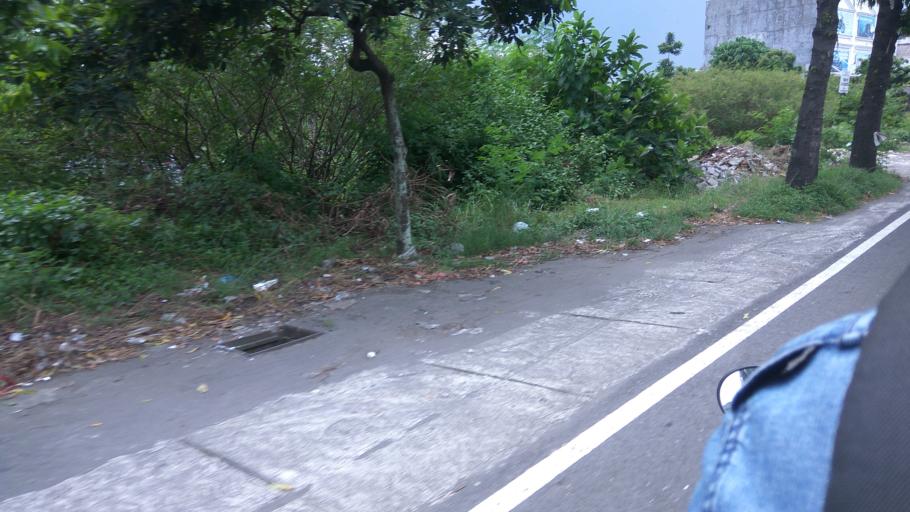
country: ID
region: Daerah Istimewa Yogyakarta
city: Melati
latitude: -7.7590
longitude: 110.3937
